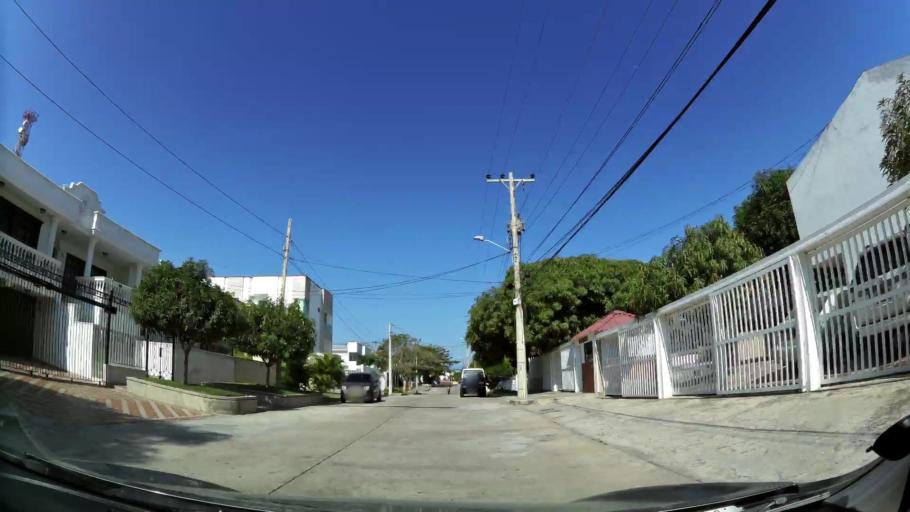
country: CO
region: Atlantico
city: Barranquilla
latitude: 10.9998
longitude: -74.8278
